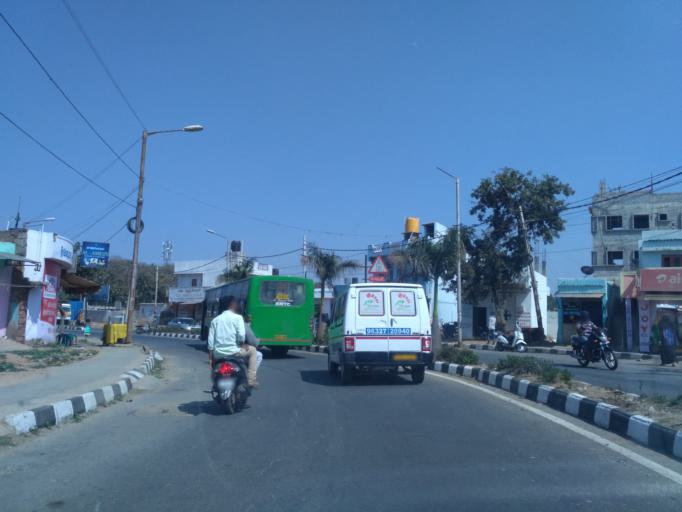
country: IN
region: Karnataka
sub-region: Bangalore Urban
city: Yelahanka
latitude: 13.0822
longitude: 77.5499
